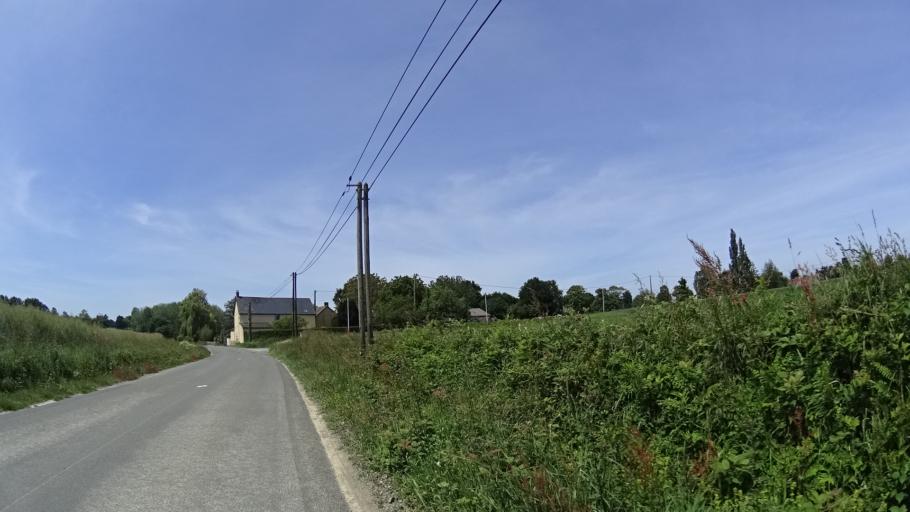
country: FR
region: Brittany
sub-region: Departement d'Ille-et-Vilaine
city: Pleumeleuc
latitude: 48.1922
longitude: -1.9052
